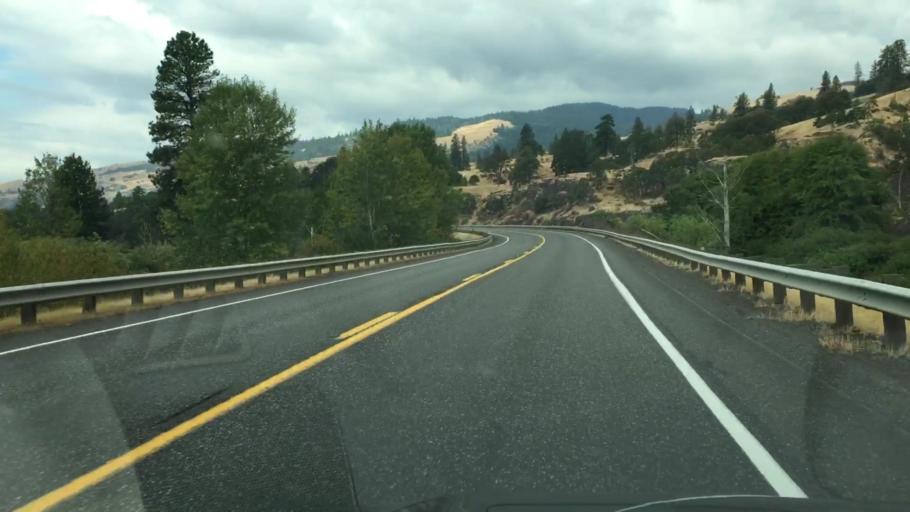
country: US
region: Oregon
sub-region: Wasco County
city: Chenoweth
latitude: 45.7100
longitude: -121.3414
